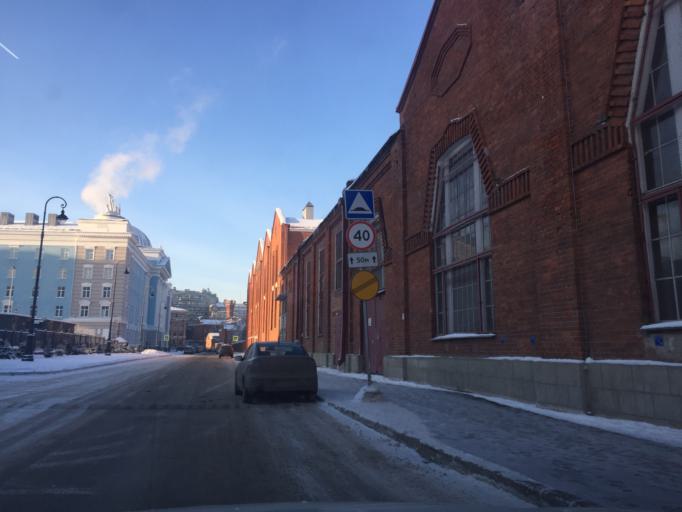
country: RU
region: St.-Petersburg
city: Petrogradka
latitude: 59.9562
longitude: 30.3354
